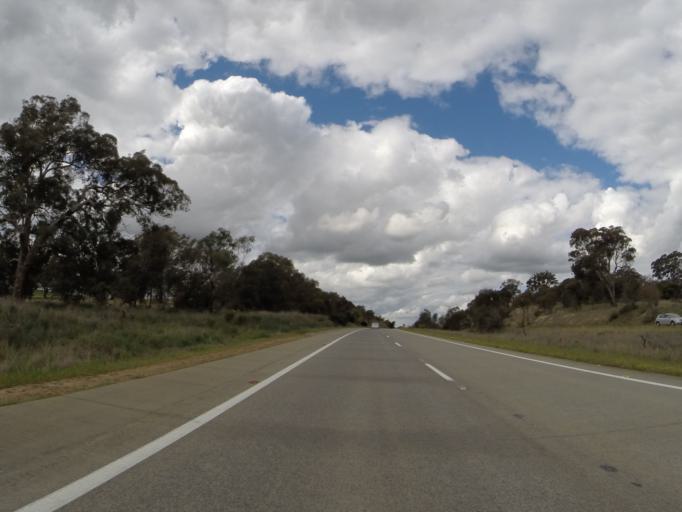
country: AU
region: New South Wales
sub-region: Yass Valley
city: Gundaroo
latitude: -34.7895
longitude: 149.2203
